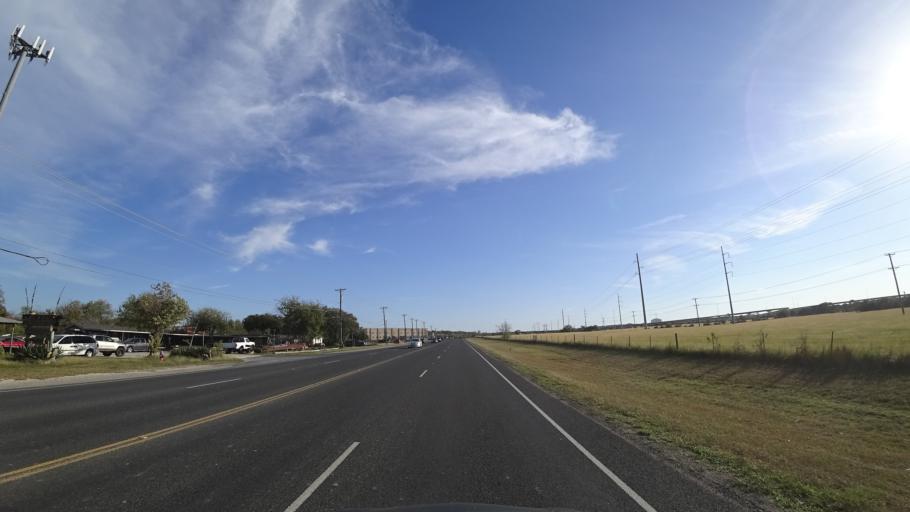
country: US
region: Texas
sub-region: Williamson County
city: Round Rock
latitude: 30.4867
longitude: -97.6956
